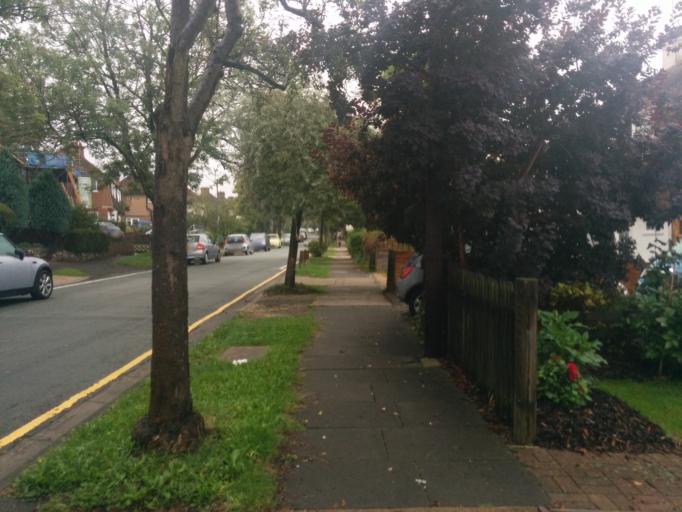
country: GB
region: England
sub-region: Surrey
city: Ewell
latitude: 51.3257
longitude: -0.2346
